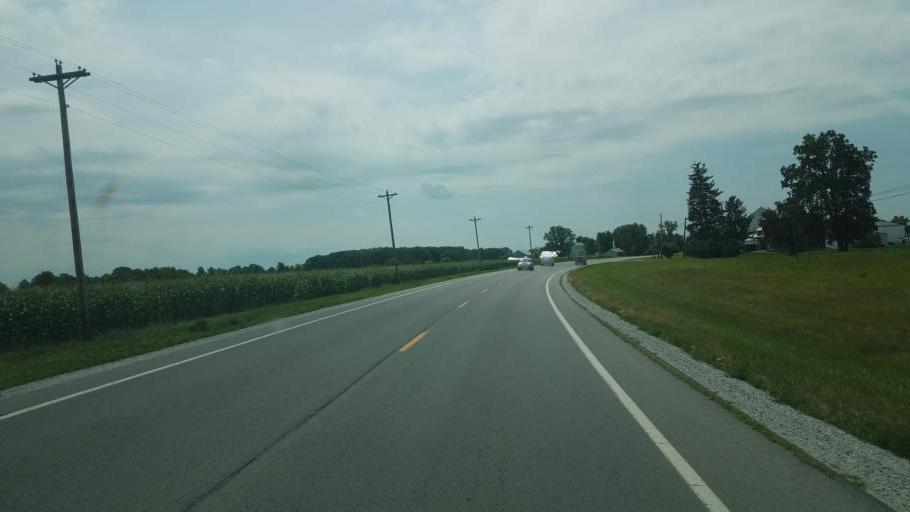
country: US
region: Ohio
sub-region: Wyandot County
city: Carey
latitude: 40.9449
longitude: -83.3542
